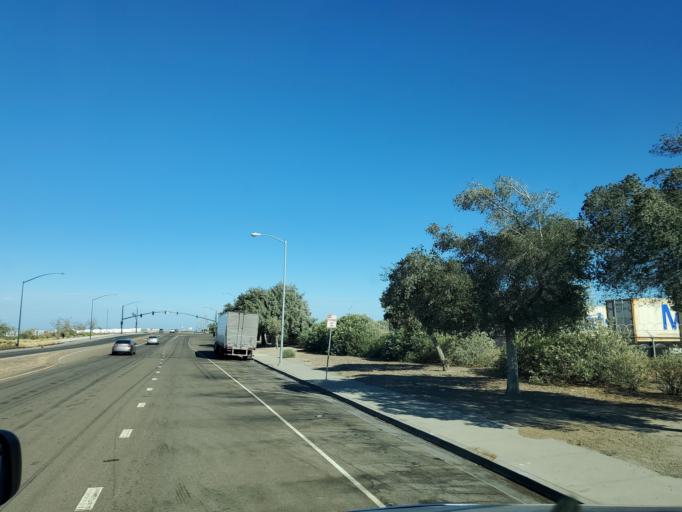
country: US
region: California
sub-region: San Joaquin County
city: Mountain House
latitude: 37.7218
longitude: -121.5204
